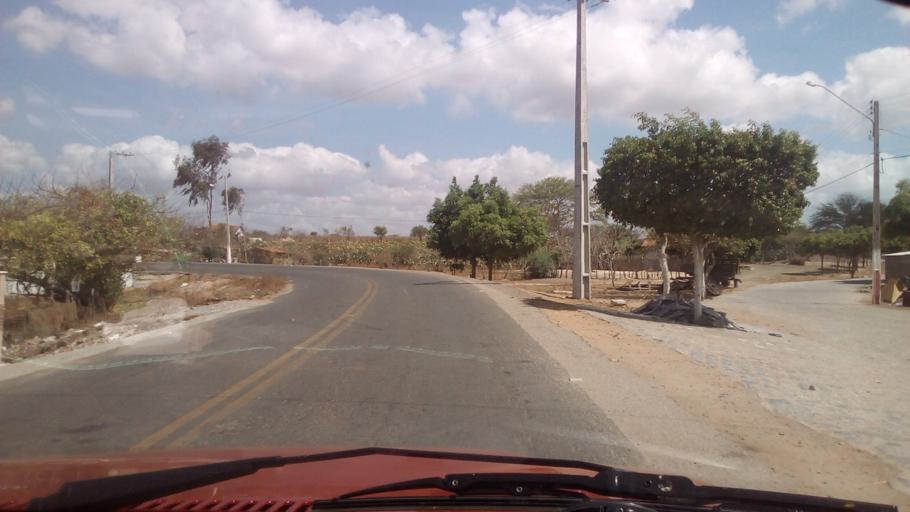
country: BR
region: Paraiba
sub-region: Dona Ines
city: Dona Ines
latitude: -6.5356
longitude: -35.6528
